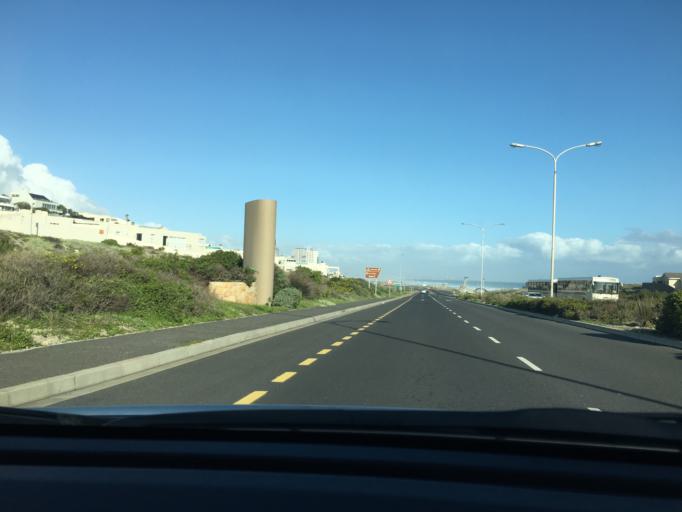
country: ZA
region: Western Cape
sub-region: City of Cape Town
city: Sunset Beach
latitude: -33.8018
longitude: 18.4636
